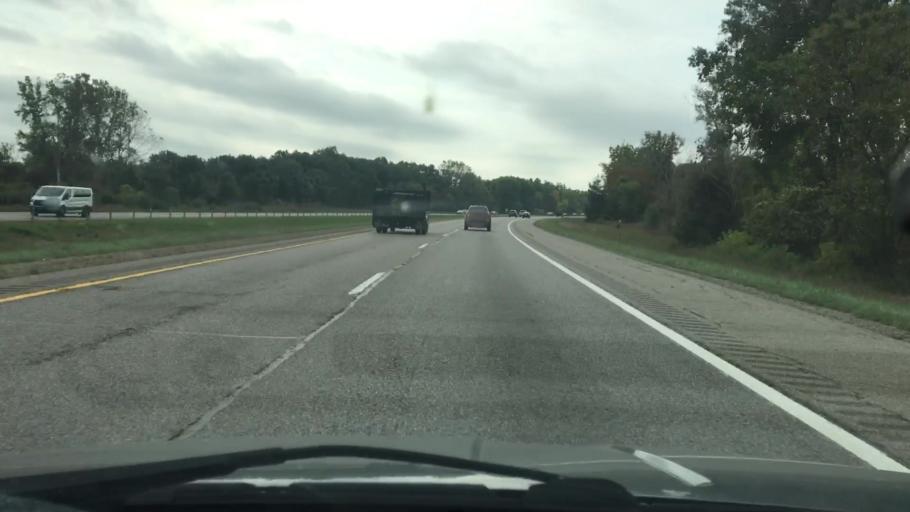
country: US
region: Michigan
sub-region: Livingston County
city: Brighton
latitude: 42.6076
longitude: -83.7413
